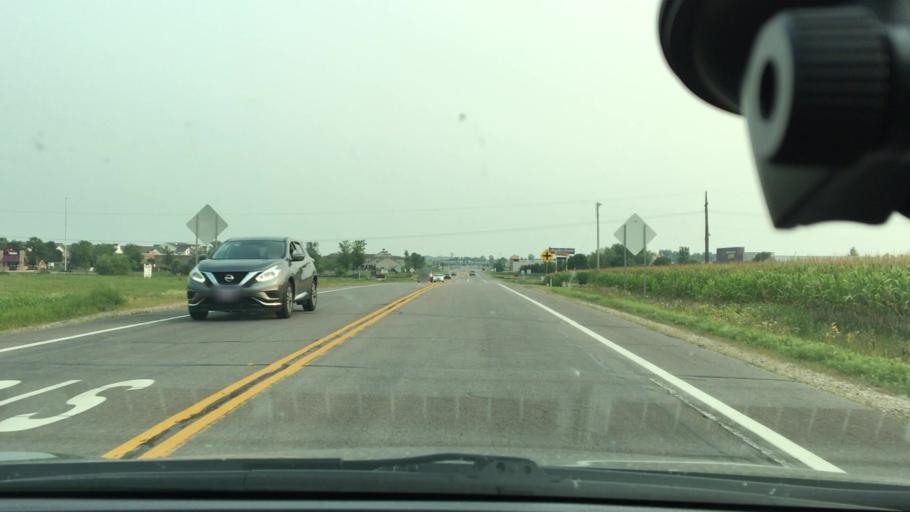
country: US
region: Minnesota
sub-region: Wright County
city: Albertville
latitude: 45.2504
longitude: -93.6633
